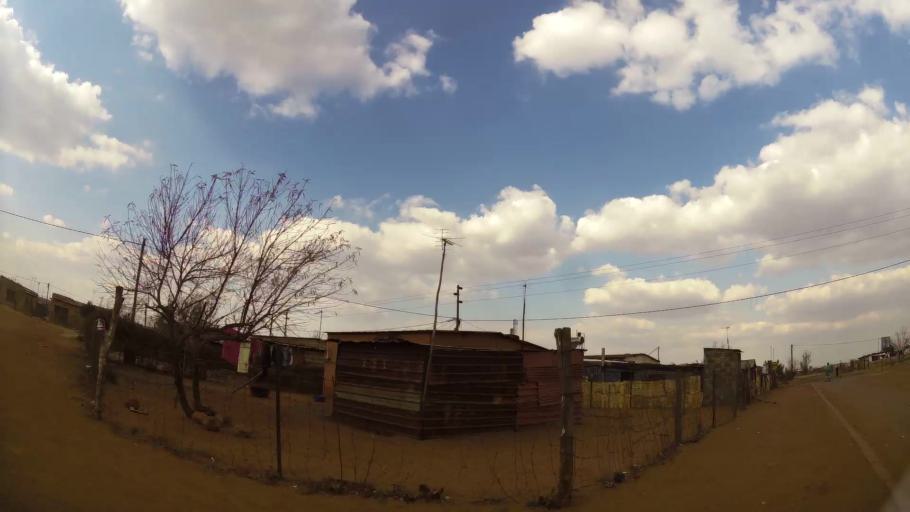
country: ZA
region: Mpumalanga
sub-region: Nkangala District Municipality
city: Delmas
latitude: -26.1394
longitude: 28.6954
